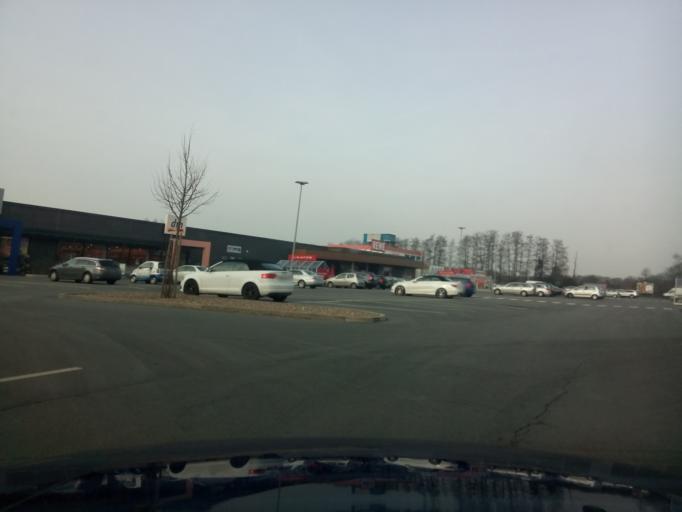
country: DE
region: Lower Saxony
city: Langen
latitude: 53.6166
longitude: 8.5975
